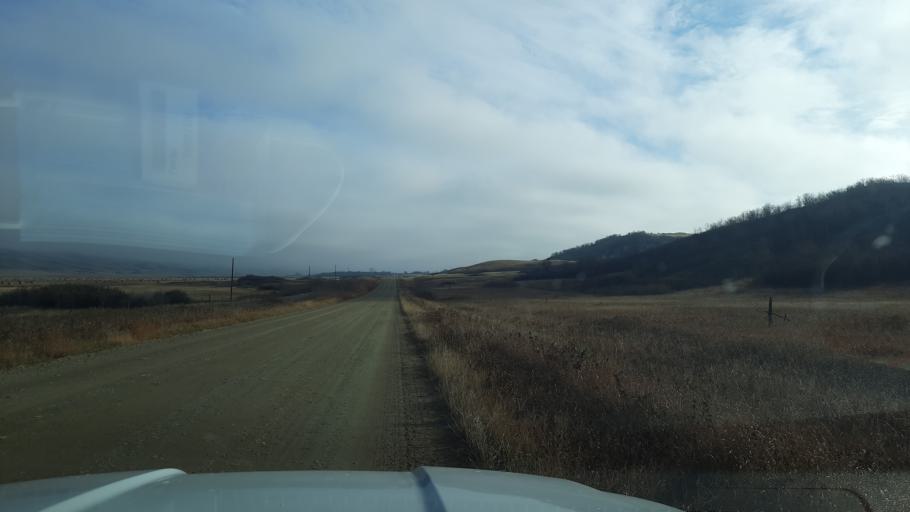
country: CA
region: Saskatchewan
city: Pilot Butte
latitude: 50.7845
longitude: -104.2053
